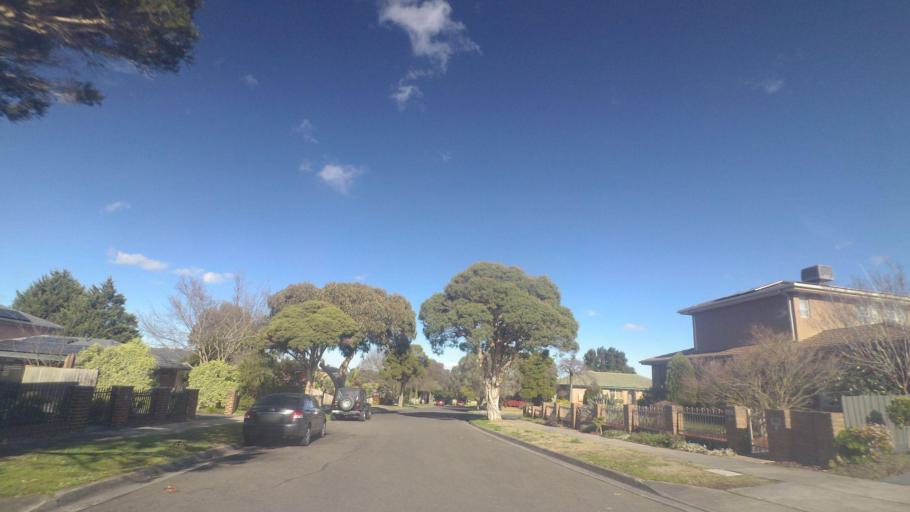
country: AU
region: Victoria
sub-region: Knox
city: Scoresby
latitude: -37.9126
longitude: 145.2488
